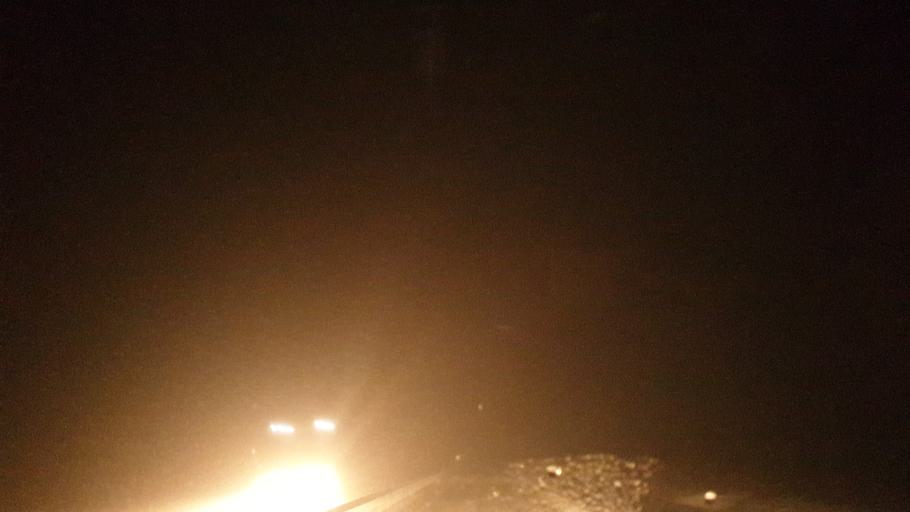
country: FI
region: Northern Ostrobothnia
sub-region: Oulunkaari
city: Kuivaniemi
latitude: 65.6253
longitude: 25.1415
